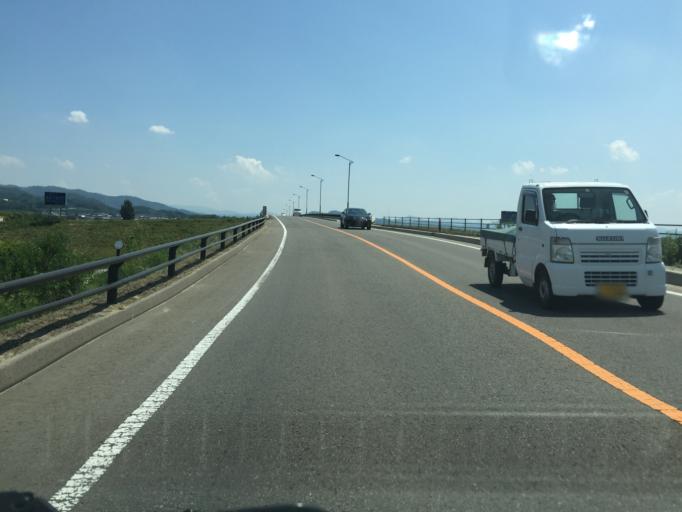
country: JP
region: Fukushima
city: Yanagawamachi-saiwaicho
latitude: 37.8717
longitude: 140.6083
